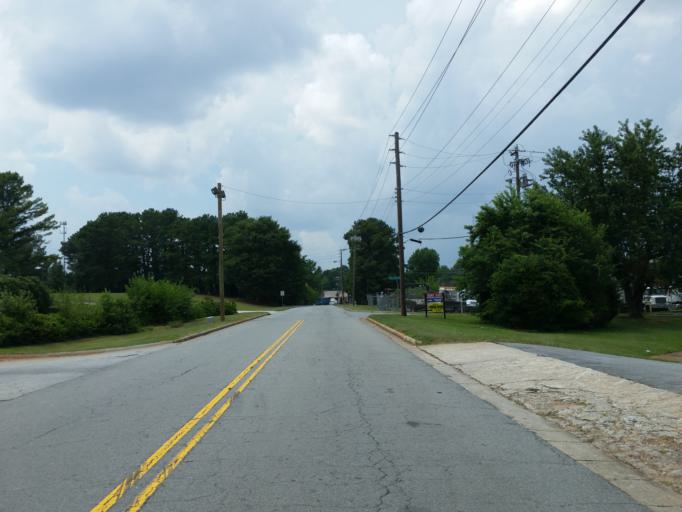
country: US
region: Georgia
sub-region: Cobb County
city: Marietta
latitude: 33.9760
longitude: -84.5403
